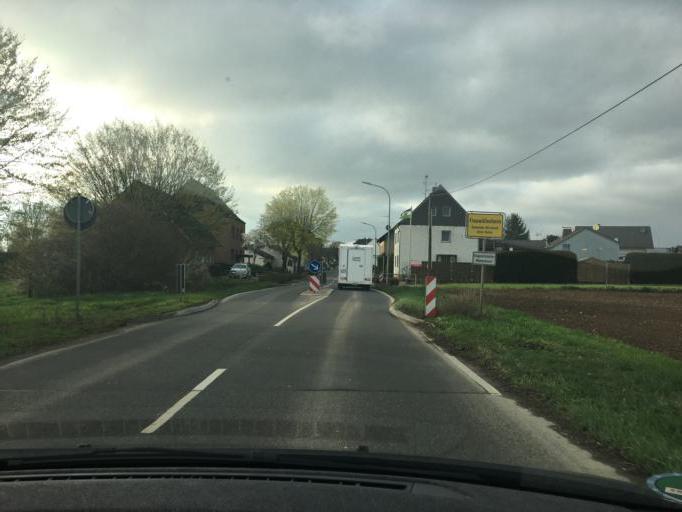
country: DE
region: North Rhine-Westphalia
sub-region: Regierungsbezirk Koln
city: Merzenich
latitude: 50.7910
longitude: 6.5748
